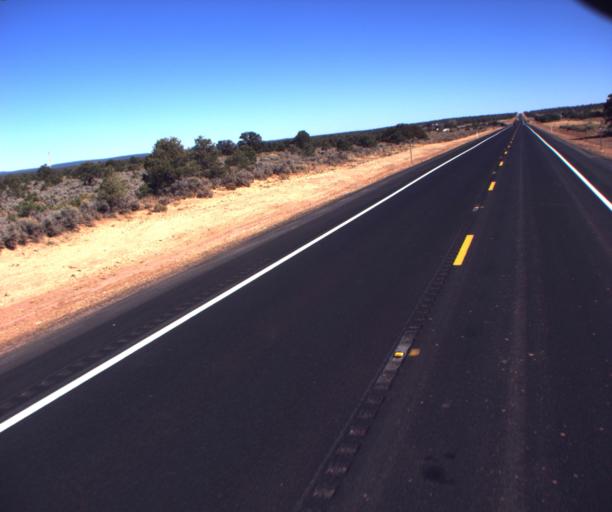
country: US
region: Arizona
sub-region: Apache County
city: Ganado
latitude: 35.7173
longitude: -109.4077
